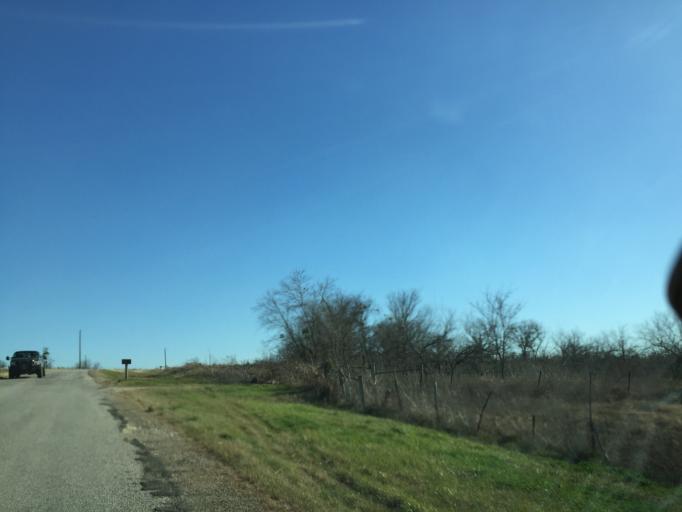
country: US
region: Texas
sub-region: Williamson County
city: Taylor
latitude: 30.5752
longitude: -97.3126
